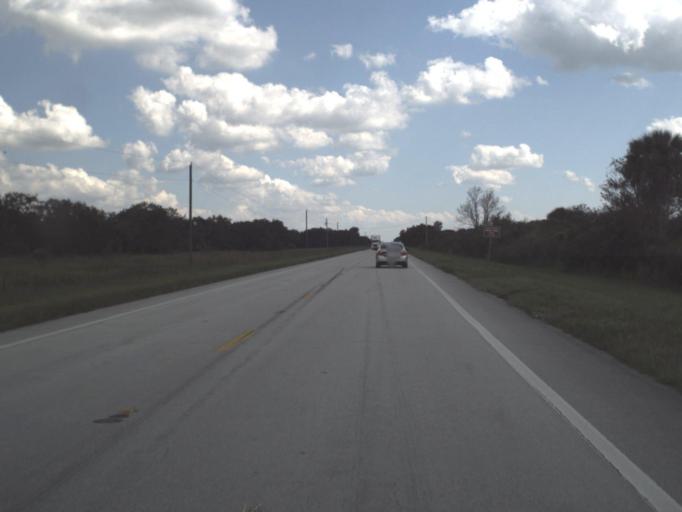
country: US
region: Florida
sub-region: Highlands County
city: Lake Placid
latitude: 27.4053
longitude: -81.1746
